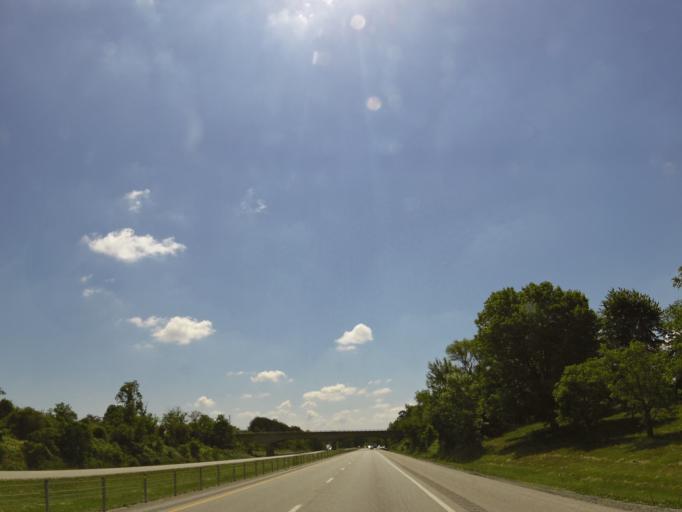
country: US
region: Kentucky
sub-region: Laurel County
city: London
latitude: 37.2059
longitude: -84.1667
